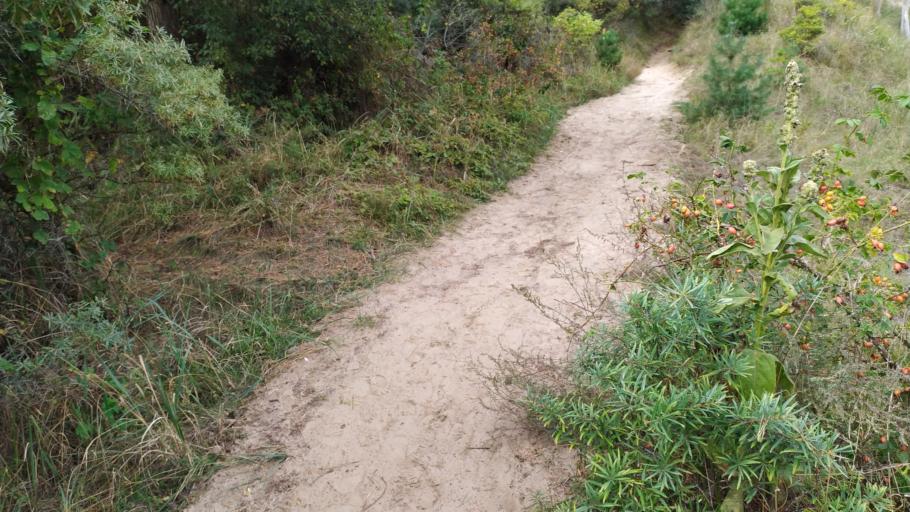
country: DE
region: Mecklenburg-Vorpommern
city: Lassan
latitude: 54.0023
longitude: 13.8560
